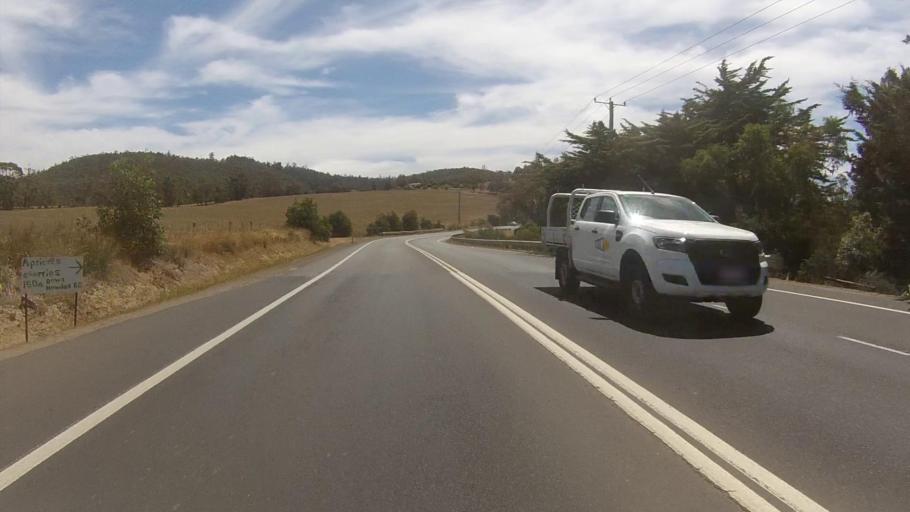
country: AU
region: Tasmania
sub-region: Kingborough
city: Margate
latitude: -43.0102
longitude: 147.2721
